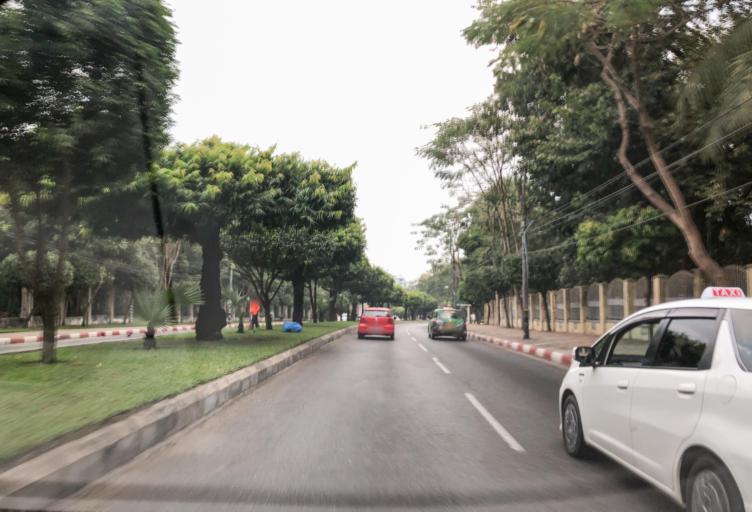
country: MM
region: Yangon
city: Yangon
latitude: 16.8004
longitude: 96.1449
